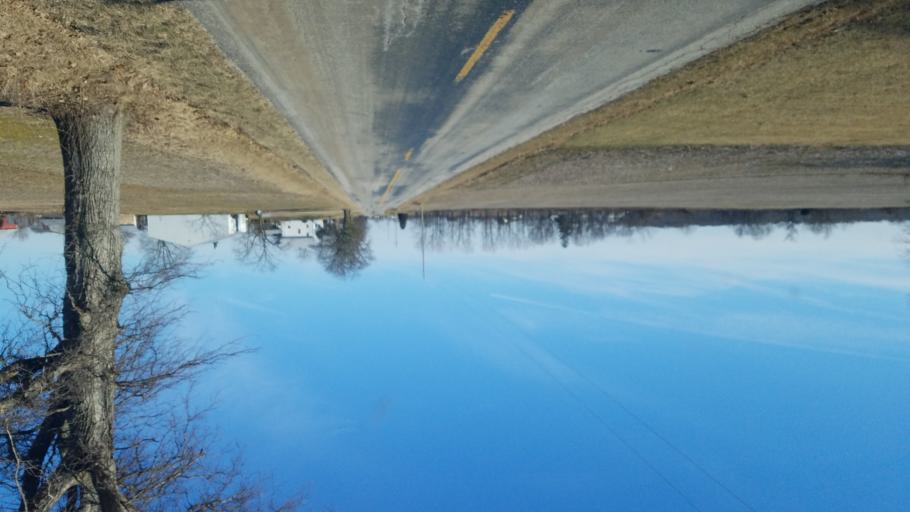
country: US
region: Ohio
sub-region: Union County
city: Richwood
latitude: 40.5151
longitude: -83.2966
